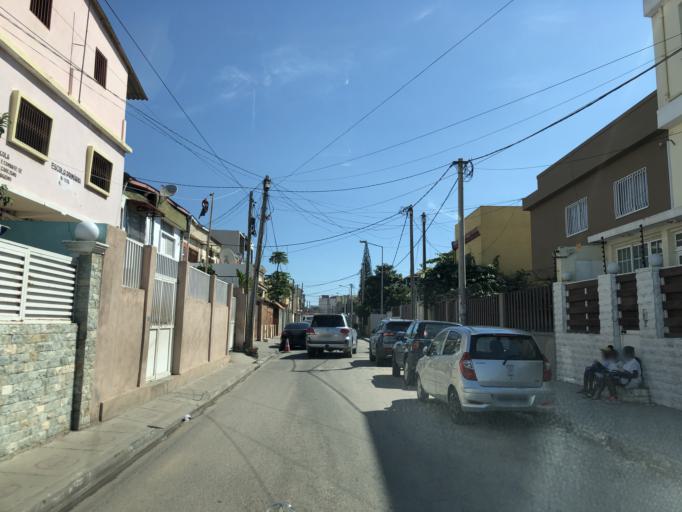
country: AO
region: Luanda
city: Luanda
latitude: -8.8461
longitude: 13.2298
